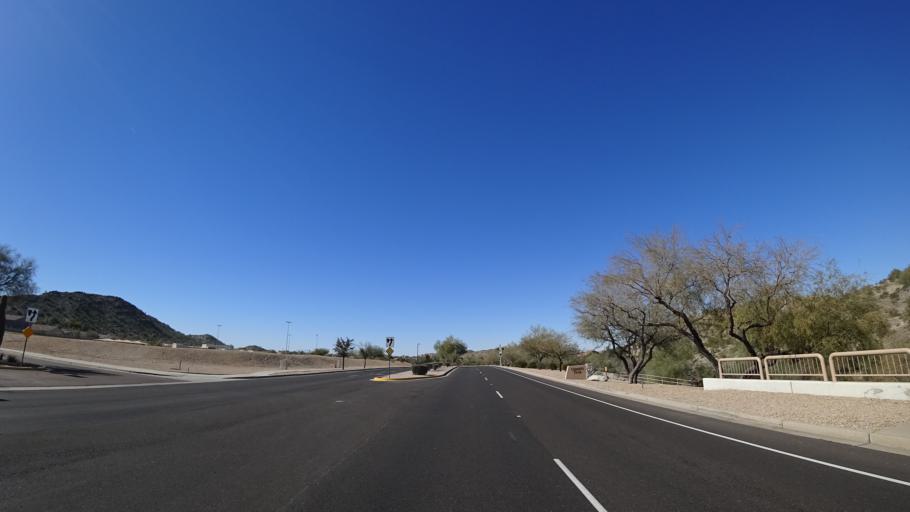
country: US
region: Arizona
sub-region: Maricopa County
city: Goodyear
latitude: 33.3553
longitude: -112.4391
